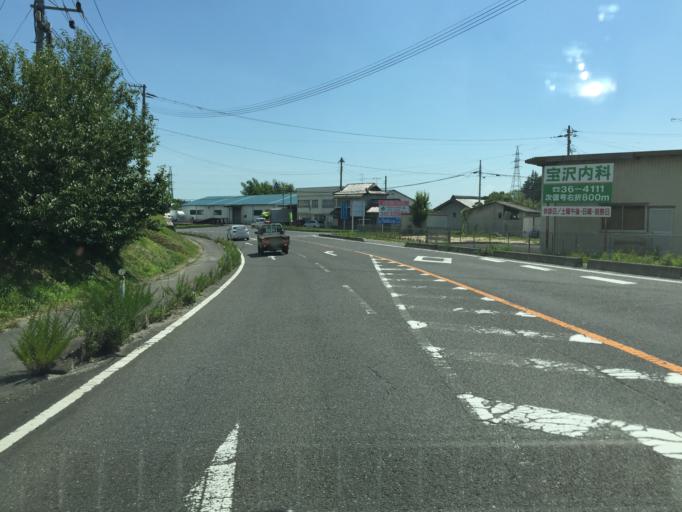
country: JP
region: Fukushima
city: Koriyama
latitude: 37.4356
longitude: 140.3905
